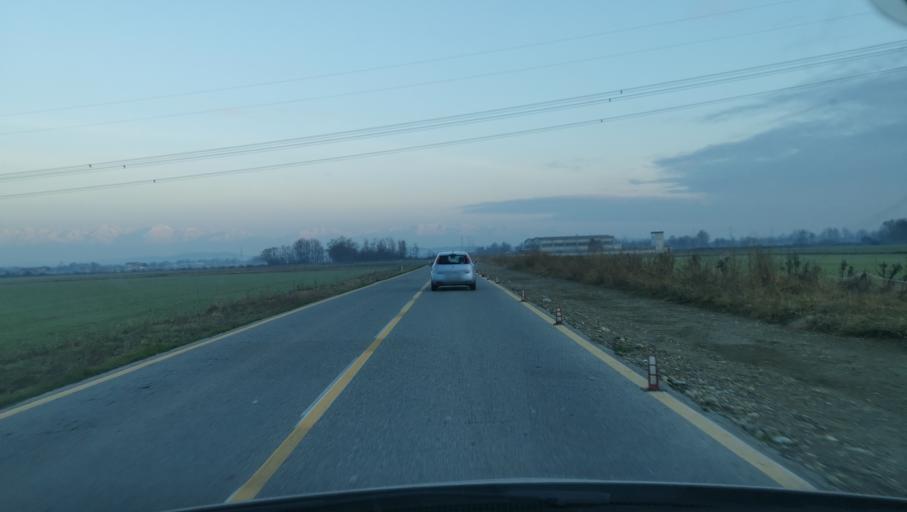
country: IT
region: Piedmont
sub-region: Provincia di Torino
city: Montanaro
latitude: 45.2581
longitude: 7.8920
